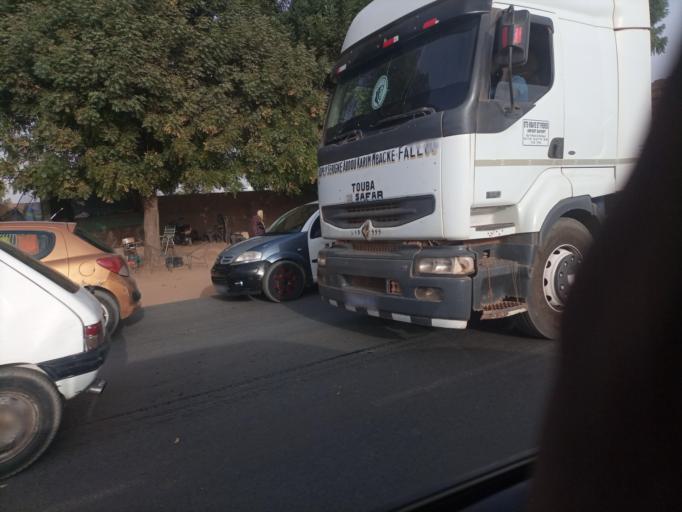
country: SN
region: Thies
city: Nguekhokh
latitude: 14.4425
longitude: -16.9794
